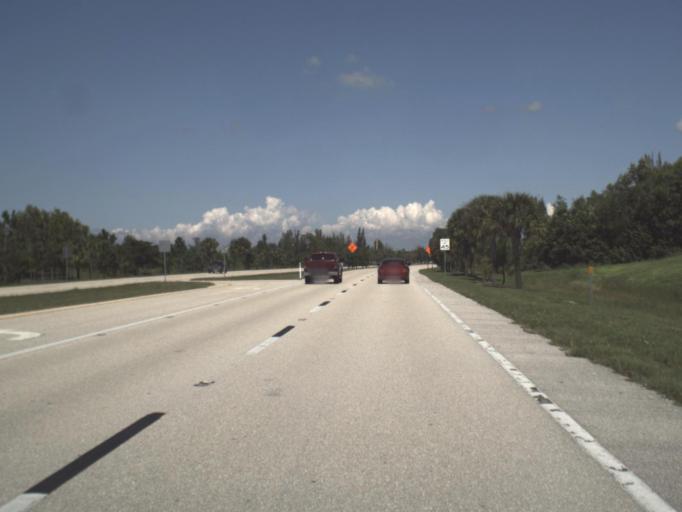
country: US
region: Florida
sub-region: Lee County
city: Pine Island Center
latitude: 26.6328
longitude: -82.0404
